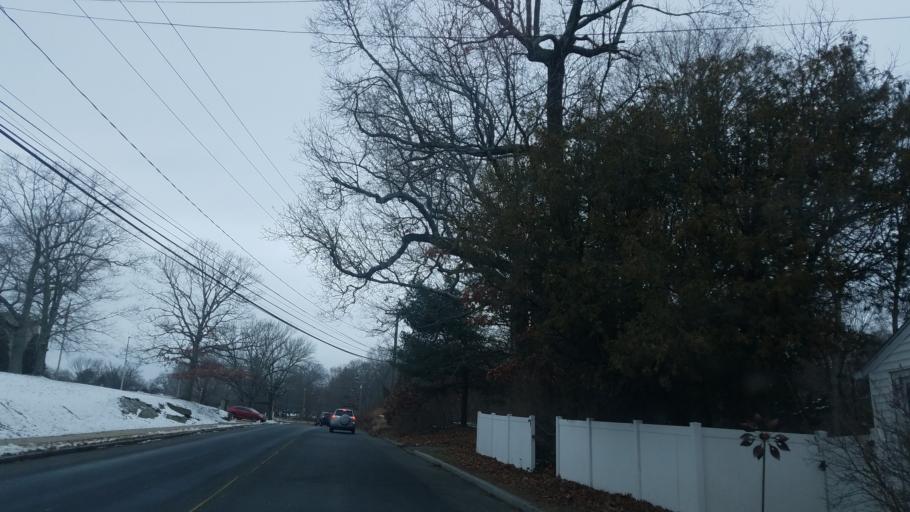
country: US
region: Connecticut
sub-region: New London County
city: Central Waterford
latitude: 41.3596
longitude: -72.1199
